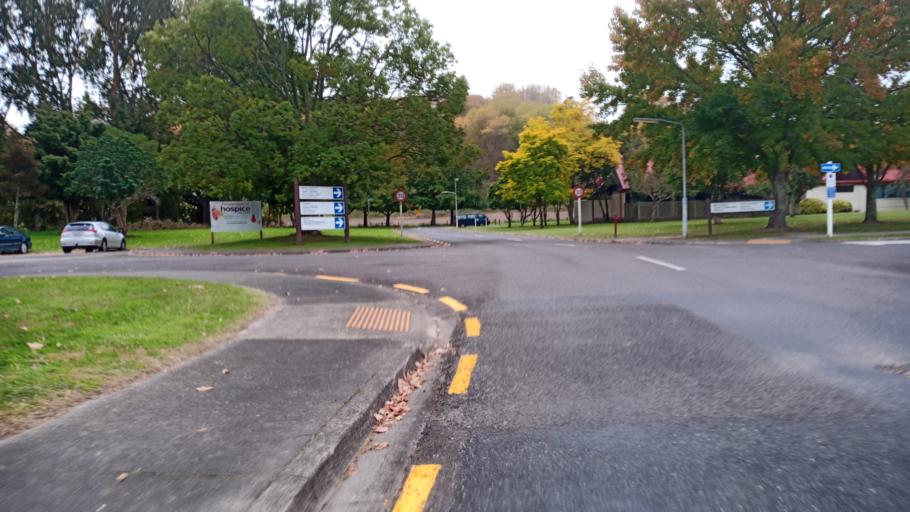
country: NZ
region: Gisborne
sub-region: Gisborne District
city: Gisborne
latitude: -38.6375
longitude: 178.0034
